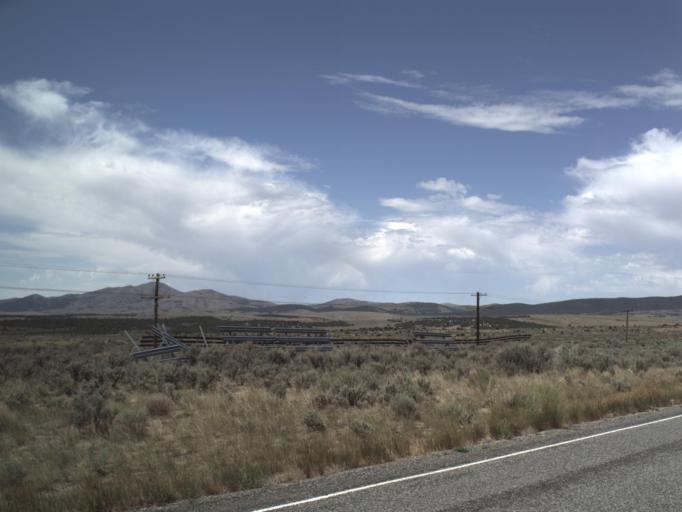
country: US
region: Utah
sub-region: Utah County
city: Genola
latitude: 39.9434
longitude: -112.1967
